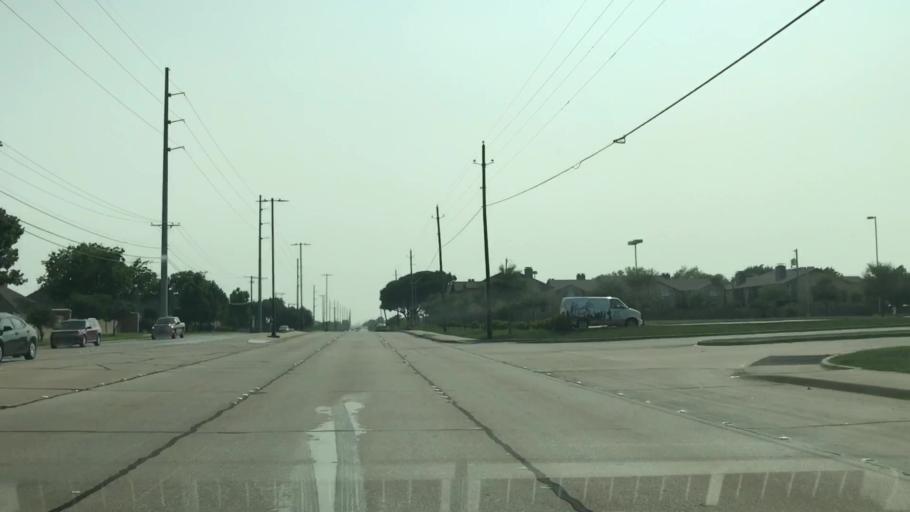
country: US
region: Texas
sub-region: Dallas County
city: Garland
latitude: 32.8915
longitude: -96.6058
